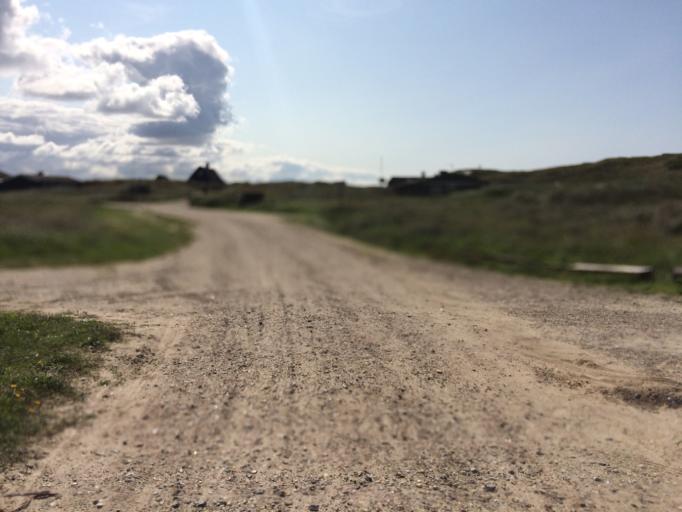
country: DK
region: Central Jutland
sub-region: Ringkobing-Skjern Kommune
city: Hvide Sande
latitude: 55.9289
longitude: 8.1508
